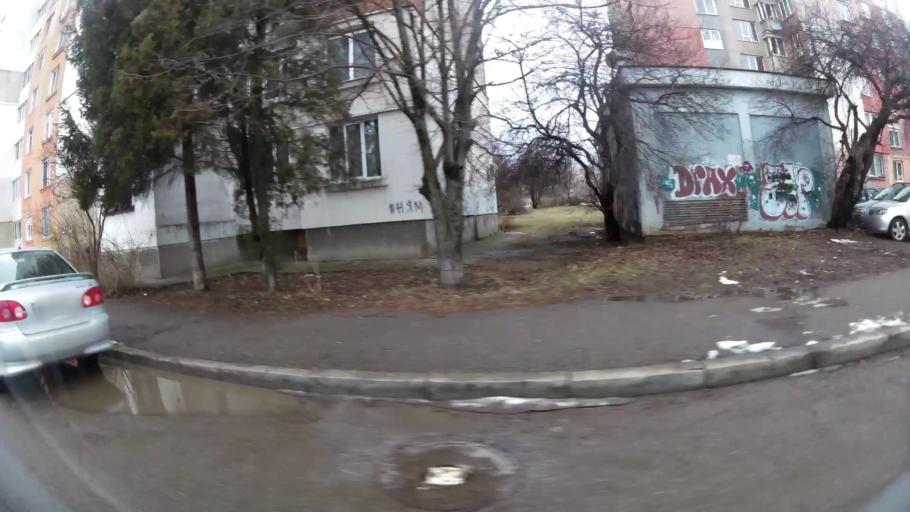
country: BG
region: Sofiya
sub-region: Obshtina Bozhurishte
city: Bozhurishte
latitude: 42.7290
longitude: 23.2550
